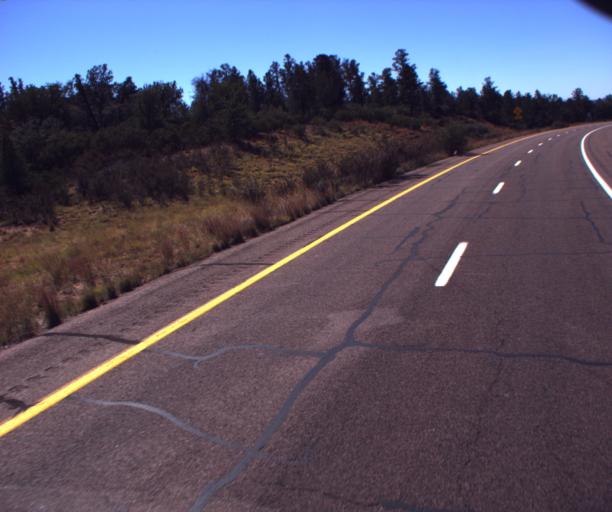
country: US
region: Arizona
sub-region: Gila County
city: Star Valley
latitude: 34.2747
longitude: -111.1758
